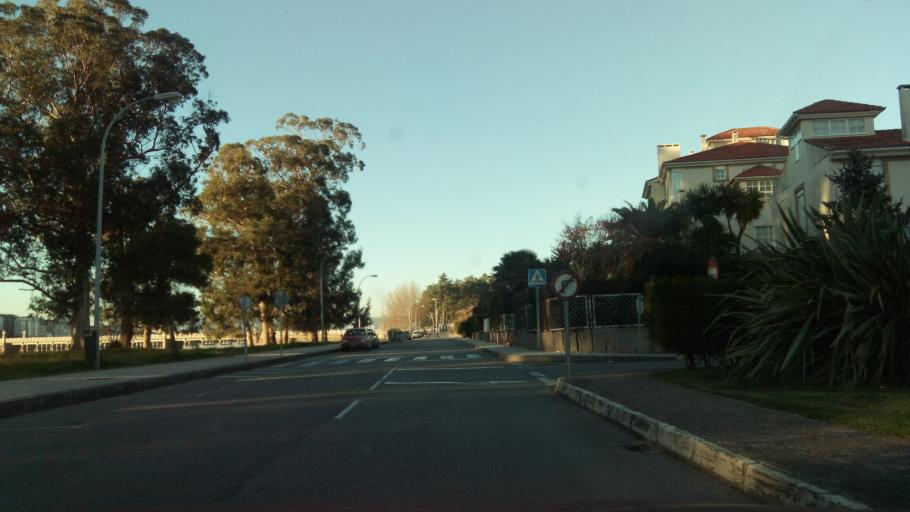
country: ES
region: Galicia
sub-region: Provincia de Pontevedra
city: O Grove
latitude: 42.4849
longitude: -8.8517
